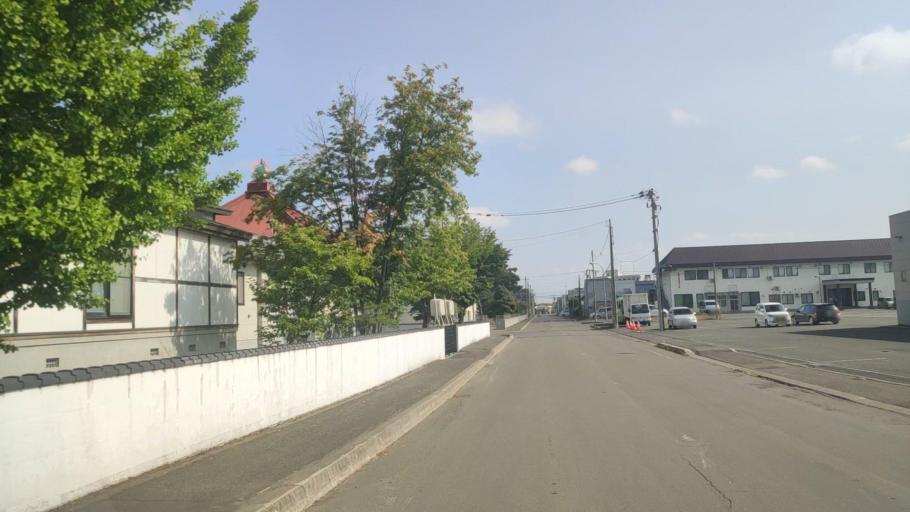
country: JP
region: Hokkaido
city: Shimo-furano
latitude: 43.3412
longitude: 142.3887
